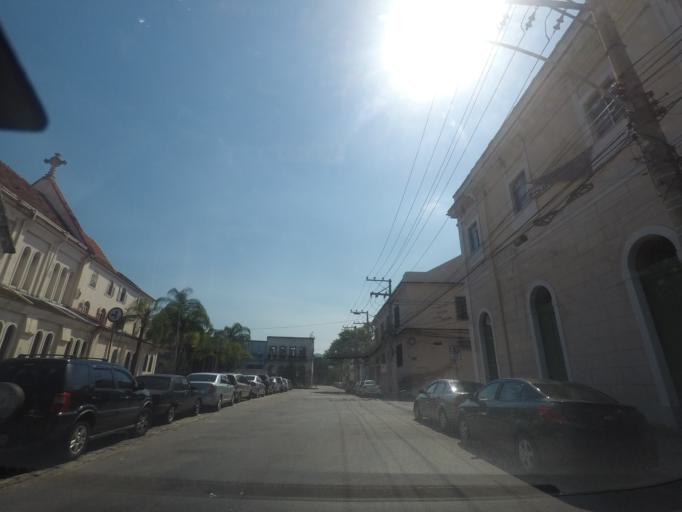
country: BR
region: Rio de Janeiro
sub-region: Rio De Janeiro
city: Rio de Janeiro
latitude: -22.8966
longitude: -43.2168
